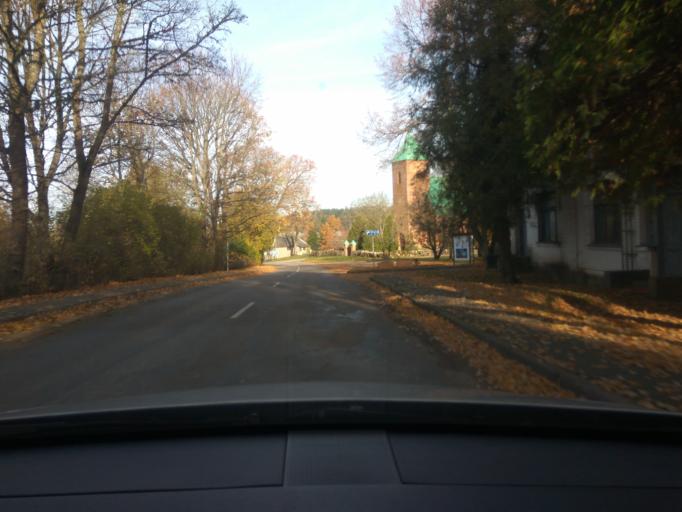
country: LV
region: Alsunga
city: Alsunga
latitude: 57.0162
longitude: 21.6883
